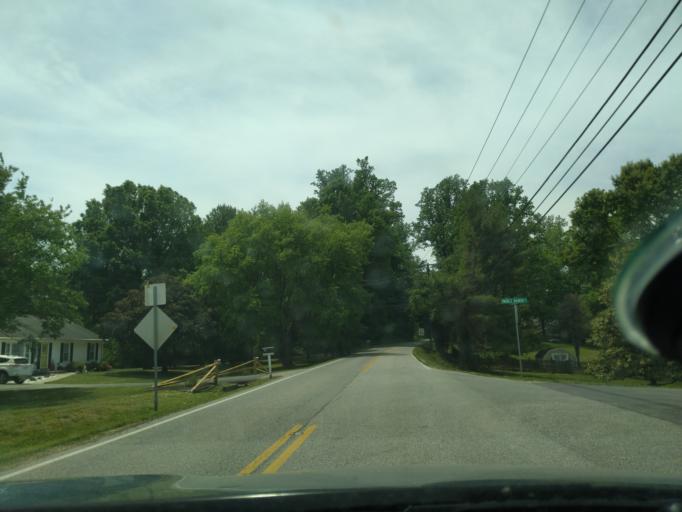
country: US
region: Maryland
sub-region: Calvert County
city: Owings
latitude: 38.7106
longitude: -76.6090
